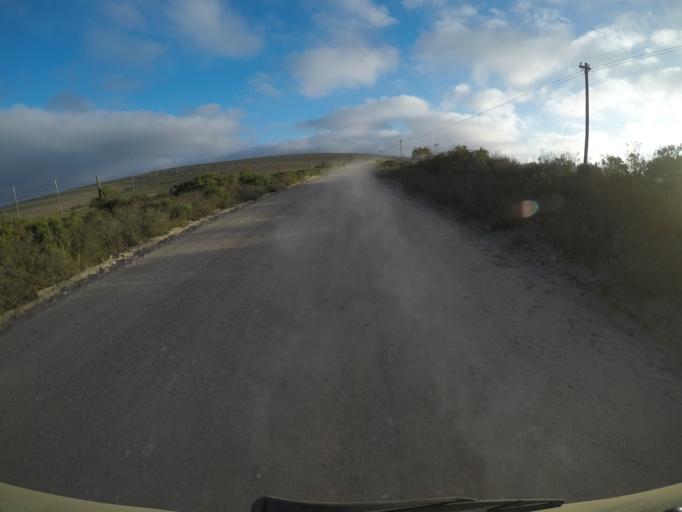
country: ZA
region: Western Cape
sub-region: Eden District Municipality
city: Mossel Bay
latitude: -34.1230
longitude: 22.0533
